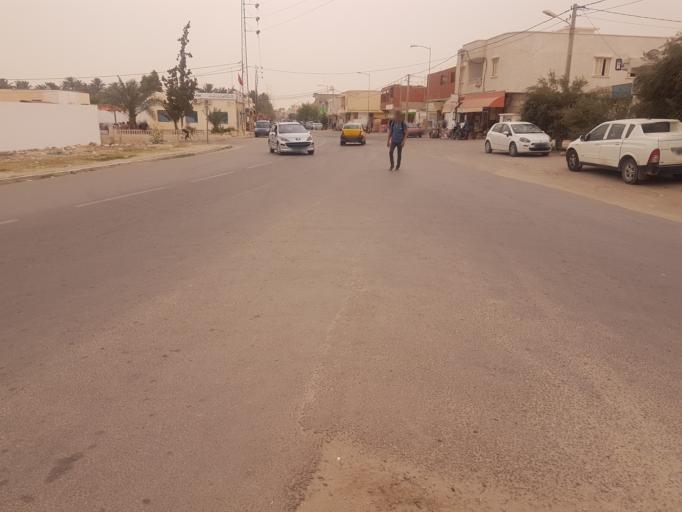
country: TN
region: Qabis
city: Gabes
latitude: 33.8788
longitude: 10.0641
